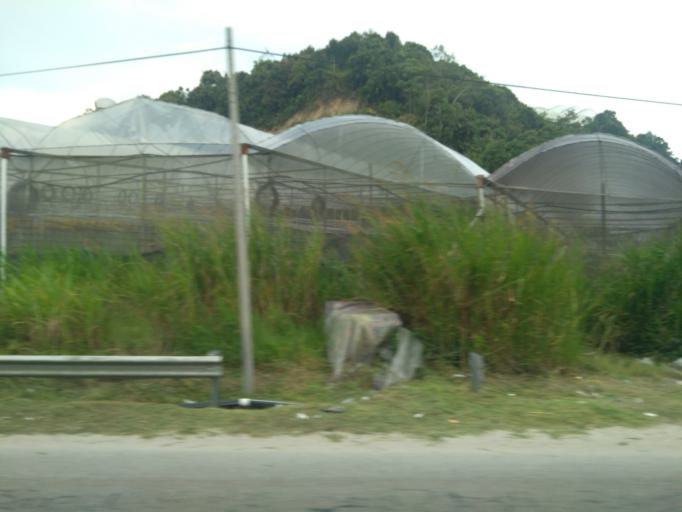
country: MY
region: Pahang
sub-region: Cameron Highlands
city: Tanah Rata
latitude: 4.5832
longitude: 101.4089
